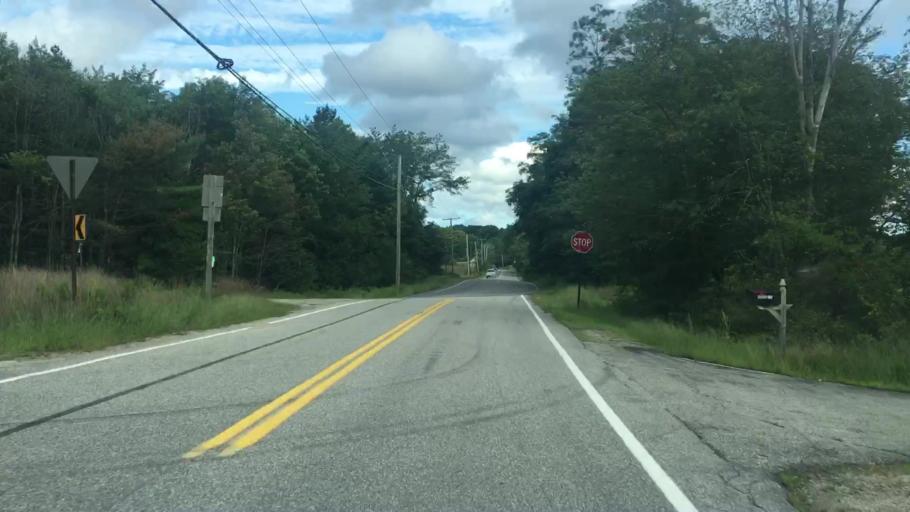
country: US
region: Maine
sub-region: York County
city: West Kennebunk
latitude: 43.4528
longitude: -70.6065
